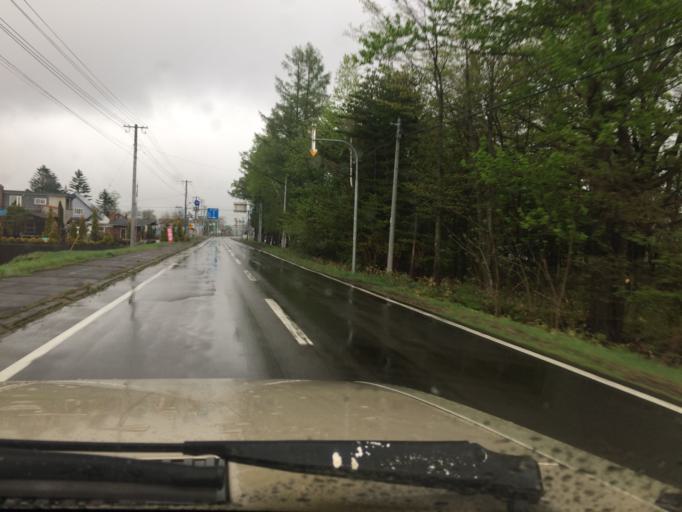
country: JP
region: Hokkaido
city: Obihiro
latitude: 42.8636
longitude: 143.0140
